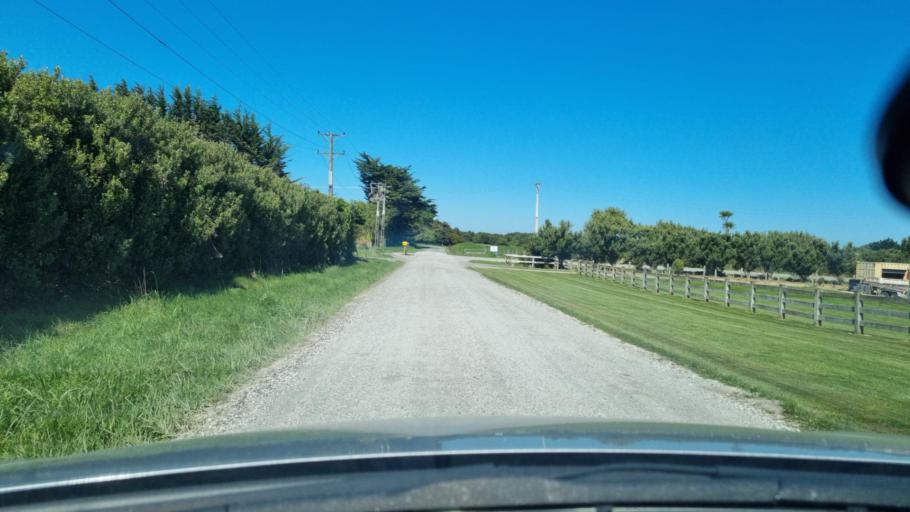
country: NZ
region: Southland
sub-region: Invercargill City
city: Invercargill
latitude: -46.4437
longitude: 168.2784
